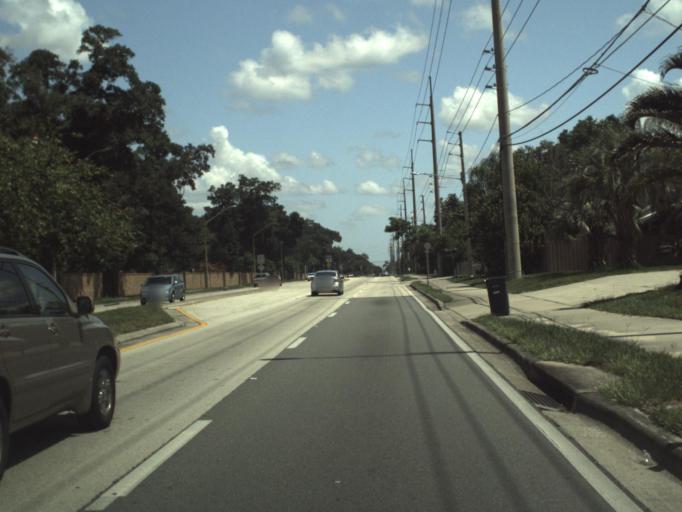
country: US
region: Florida
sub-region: Orange County
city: Conway
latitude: 28.4870
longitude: -81.3307
